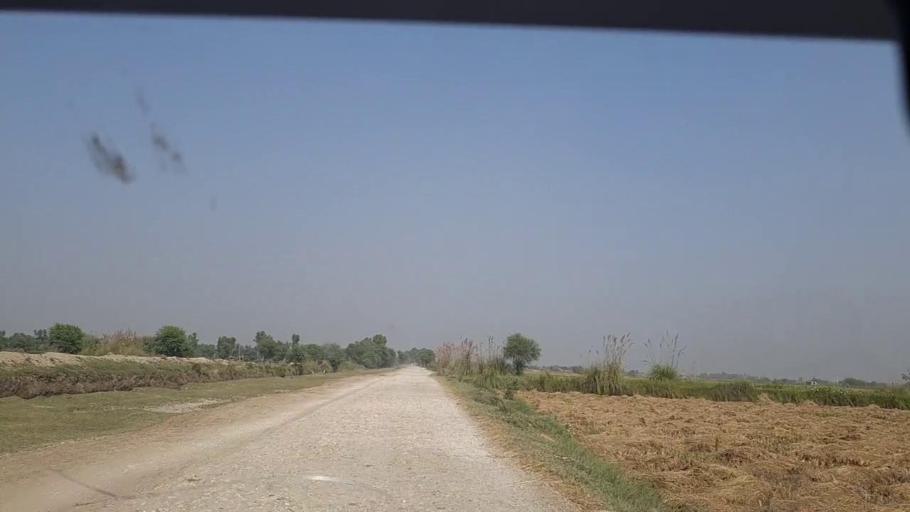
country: PK
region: Sindh
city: Shikarpur
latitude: 28.1049
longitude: 68.6902
